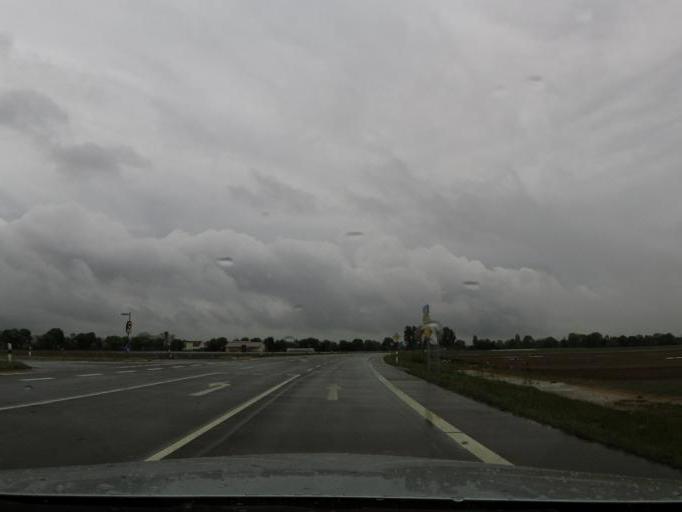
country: DE
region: Hesse
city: Weiterstadt
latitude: 49.9398
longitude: 8.5935
